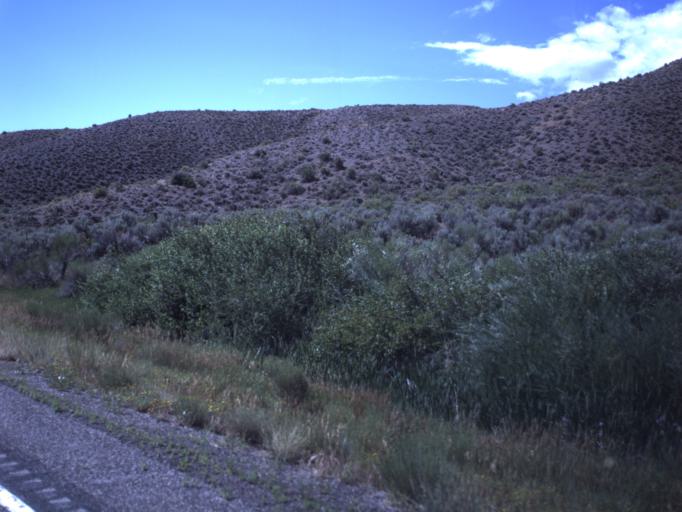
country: US
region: Utah
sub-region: Sevier County
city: Monroe
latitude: 38.4777
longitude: -112.2408
